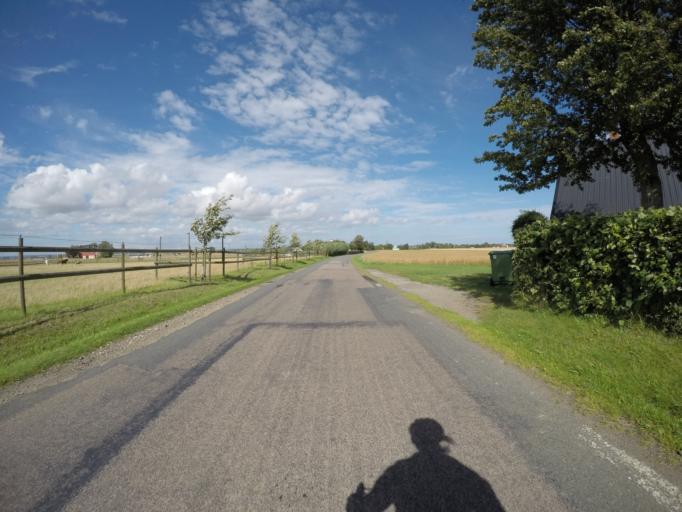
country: SE
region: Skane
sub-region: Simrishamns Kommun
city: Simrishamn
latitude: 55.4919
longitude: 14.1954
